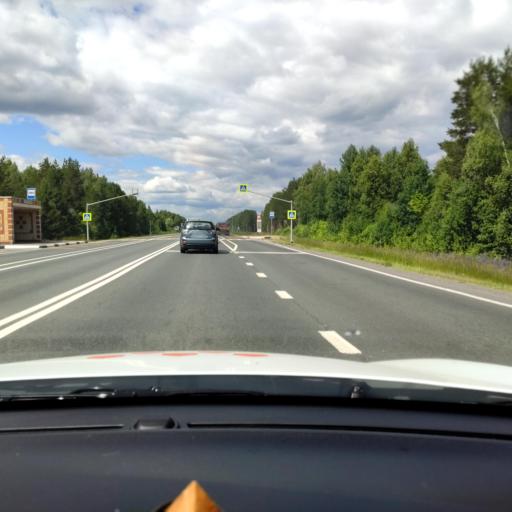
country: RU
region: Mariy-El
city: Pomary
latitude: 55.9408
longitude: 48.3707
